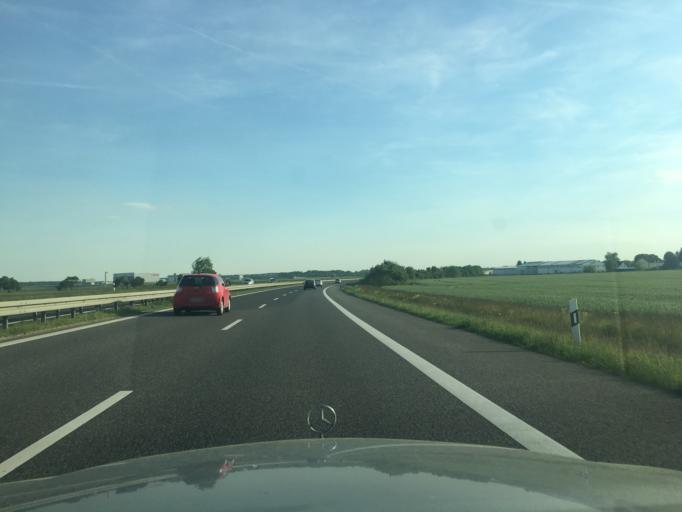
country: DE
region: Brandenburg
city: Schonefeld
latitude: 52.3741
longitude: 13.4851
